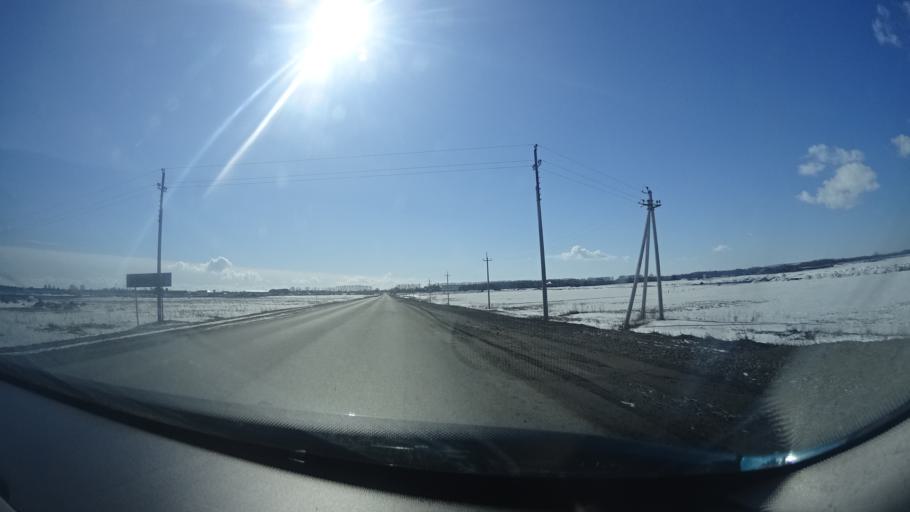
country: RU
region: Bashkortostan
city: Ufa
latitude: 54.6251
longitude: 55.8936
